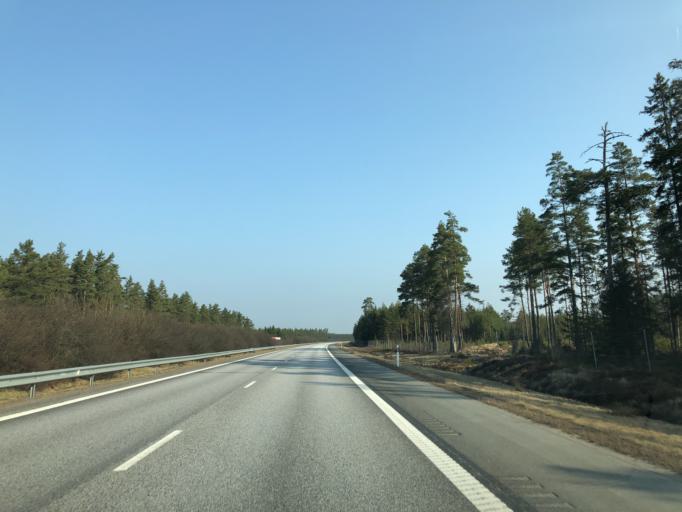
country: SE
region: Joenkoeping
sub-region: Varnamo Kommun
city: Varnamo
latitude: 57.2752
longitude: 14.0826
